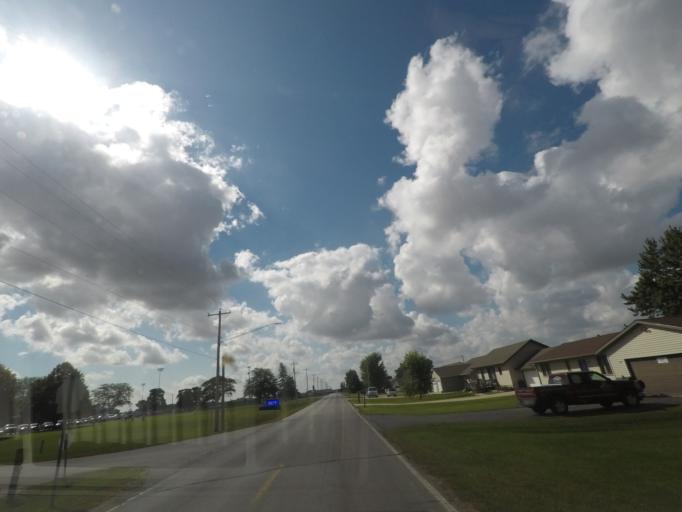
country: US
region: Iowa
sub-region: Story County
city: Nevada
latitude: 42.0113
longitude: -93.3192
